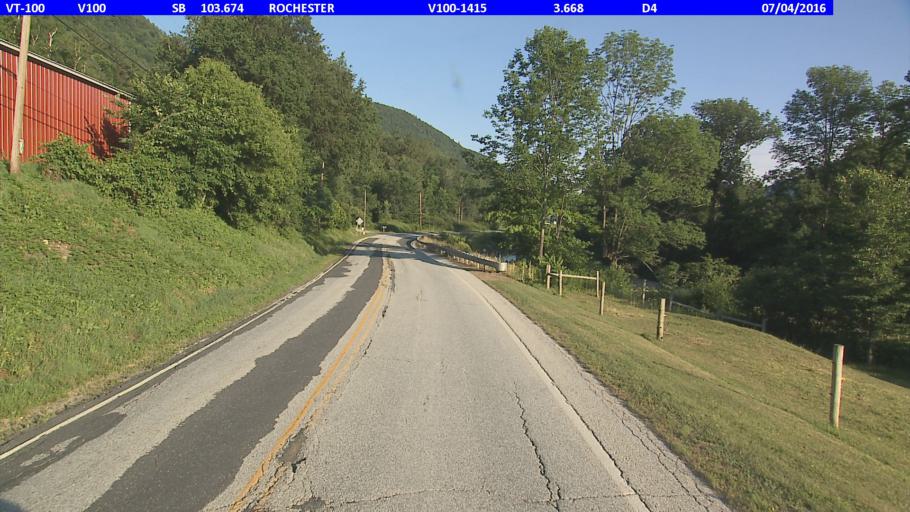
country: US
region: Vermont
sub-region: Orange County
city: Randolph
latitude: 43.8542
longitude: -72.8022
